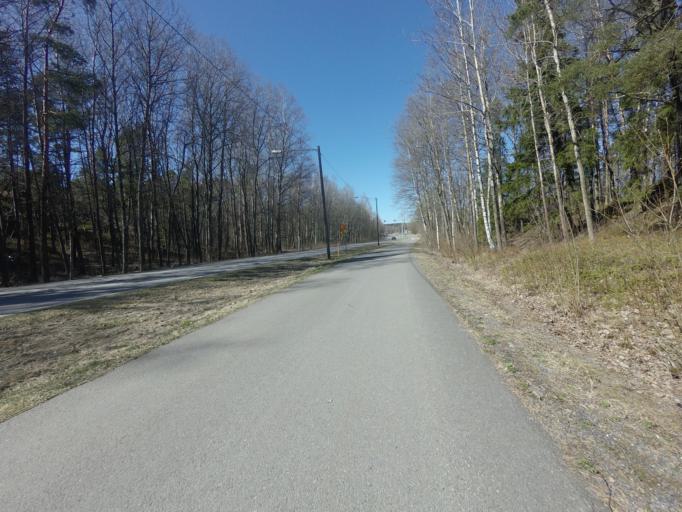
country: FI
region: Varsinais-Suomi
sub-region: Turku
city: Raisio
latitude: 60.4499
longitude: 22.1788
